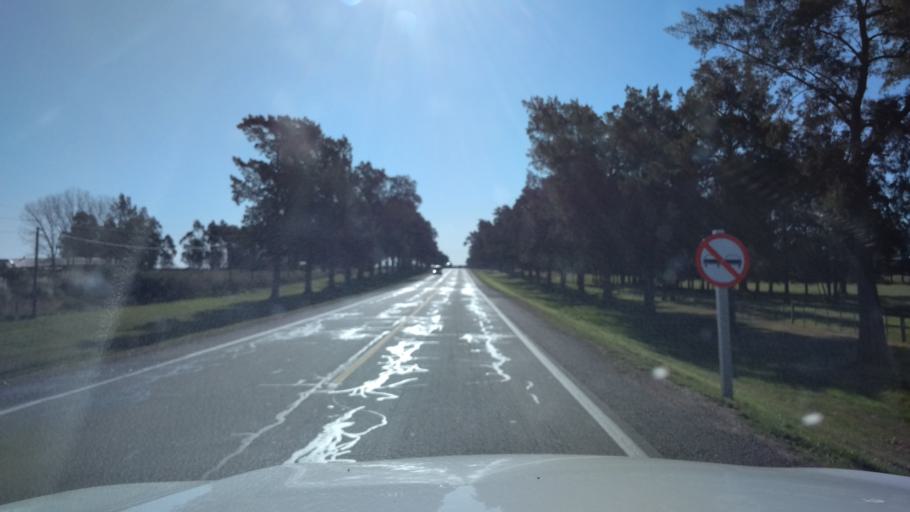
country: UY
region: Canelones
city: San Jacinto
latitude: -34.5802
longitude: -55.8446
